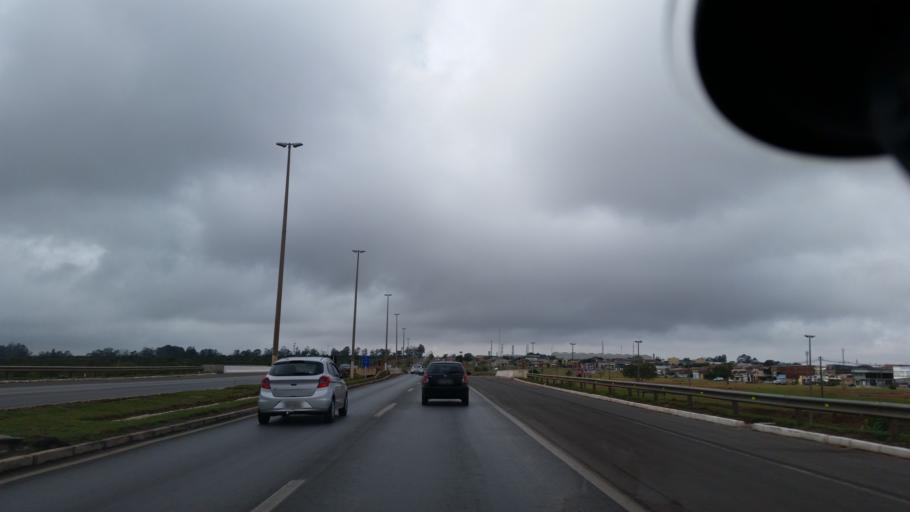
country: BR
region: Federal District
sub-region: Brasilia
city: Brasilia
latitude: -16.0027
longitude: -47.9843
